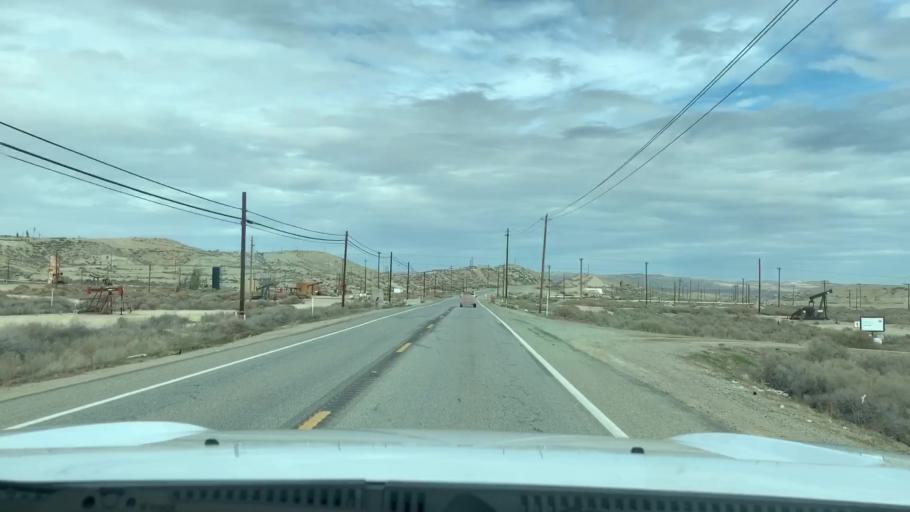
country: US
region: California
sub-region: Kern County
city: Maricopa
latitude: 35.0733
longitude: -119.4020
